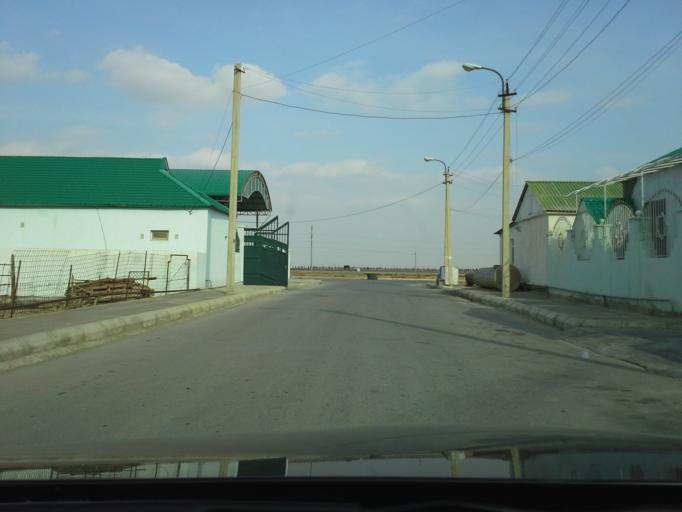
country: TM
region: Ahal
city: Abadan
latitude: 38.0415
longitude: 58.2789
